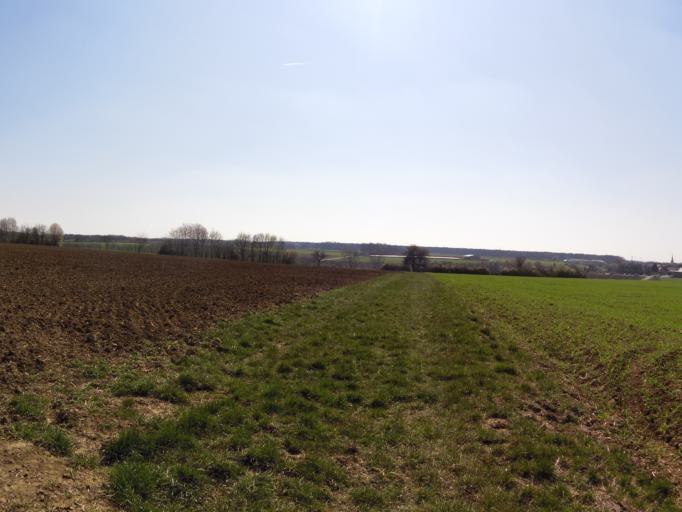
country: DE
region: Bavaria
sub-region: Regierungsbezirk Unterfranken
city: Biebelried
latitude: 49.7379
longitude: 10.0980
